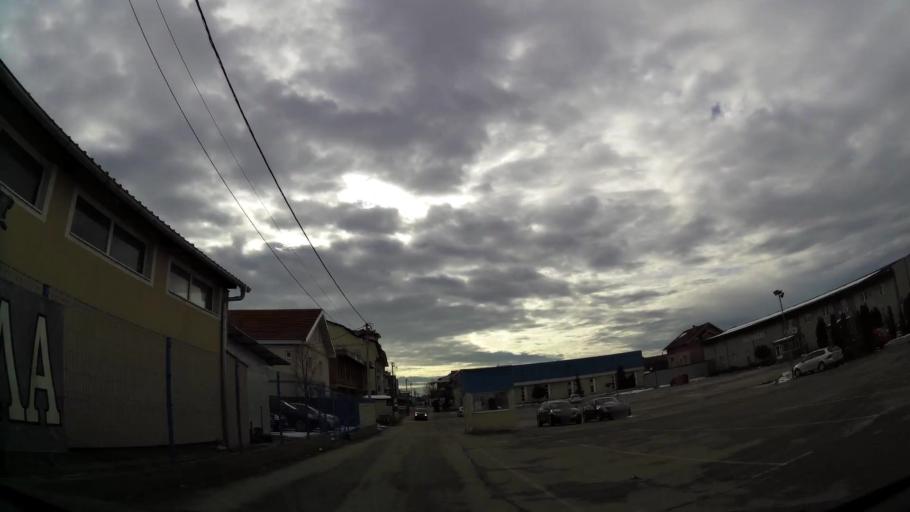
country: RS
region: Central Serbia
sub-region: Belgrade
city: Surcin
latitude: 44.8029
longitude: 20.3422
